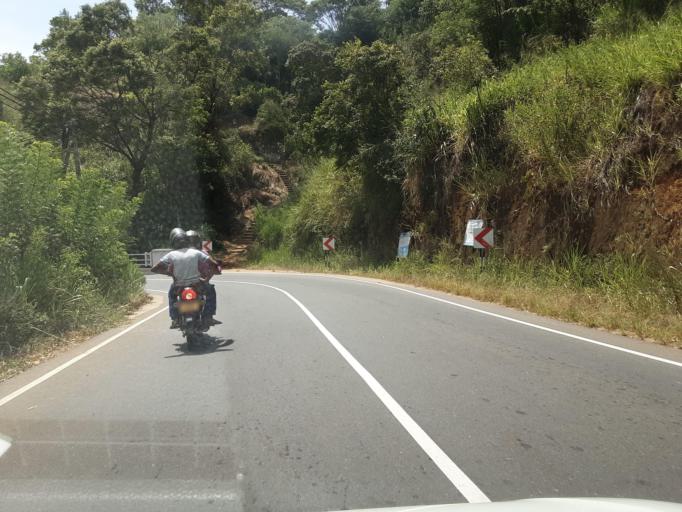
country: LK
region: Central
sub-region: Nuwara Eliya District
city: Nuwara Eliya
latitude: 6.9353
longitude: 80.9088
